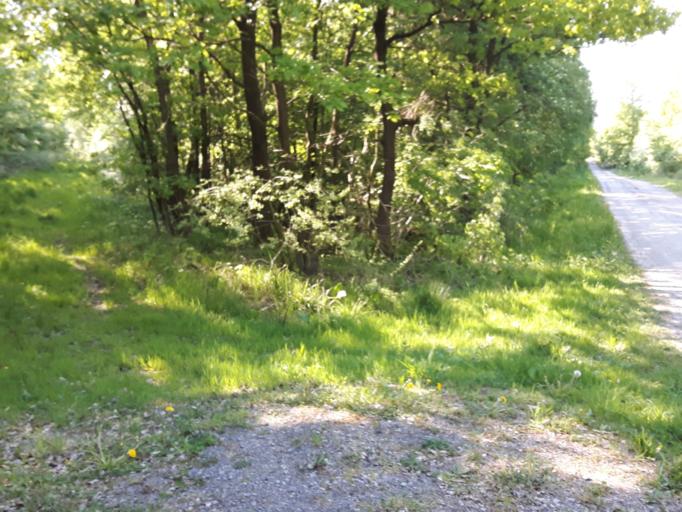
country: DE
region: Lower Saxony
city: Aerzen
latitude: 52.0963
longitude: 9.2613
